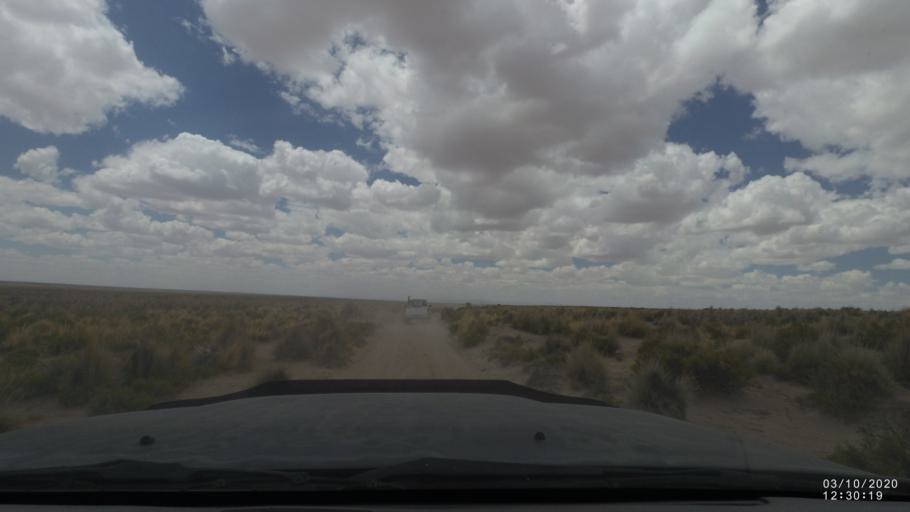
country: BO
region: Oruro
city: Poopo
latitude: -18.6872
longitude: -67.5442
